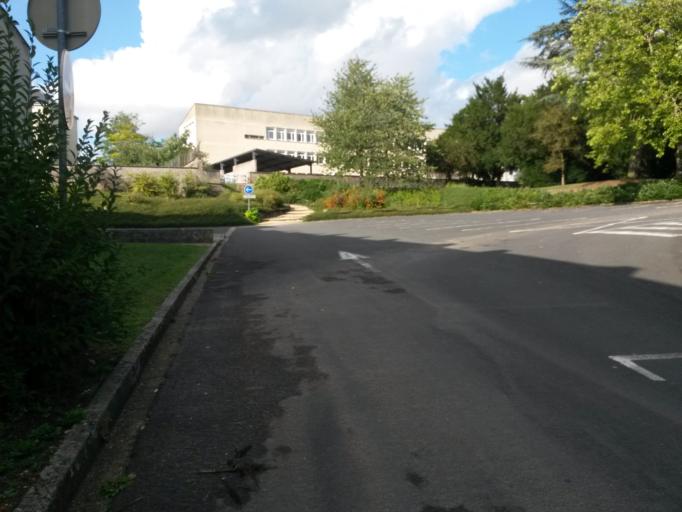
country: FR
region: Centre
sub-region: Departement du Loiret
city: Pithiviers
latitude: 48.1766
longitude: 2.2530
